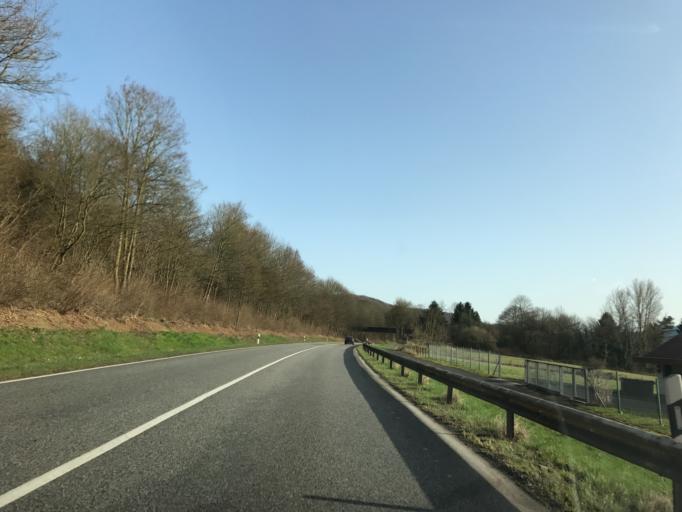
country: DE
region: Rheinland-Pfalz
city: Bad Honningen
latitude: 50.5159
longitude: 7.3219
